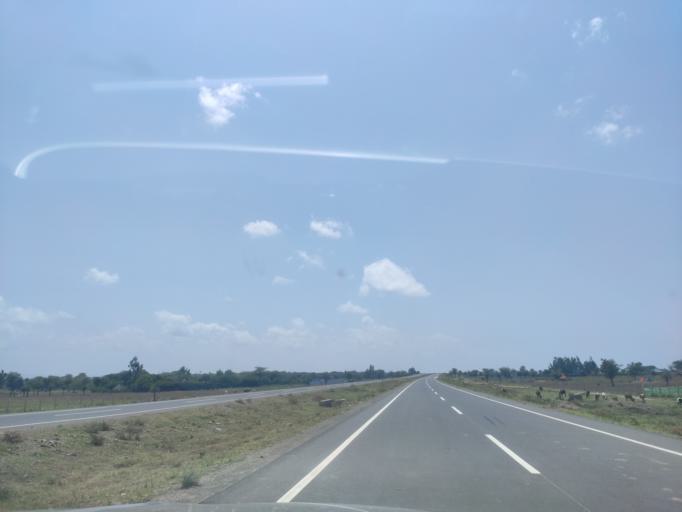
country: ET
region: Oromiya
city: Mojo
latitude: 8.3396
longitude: 38.9709
